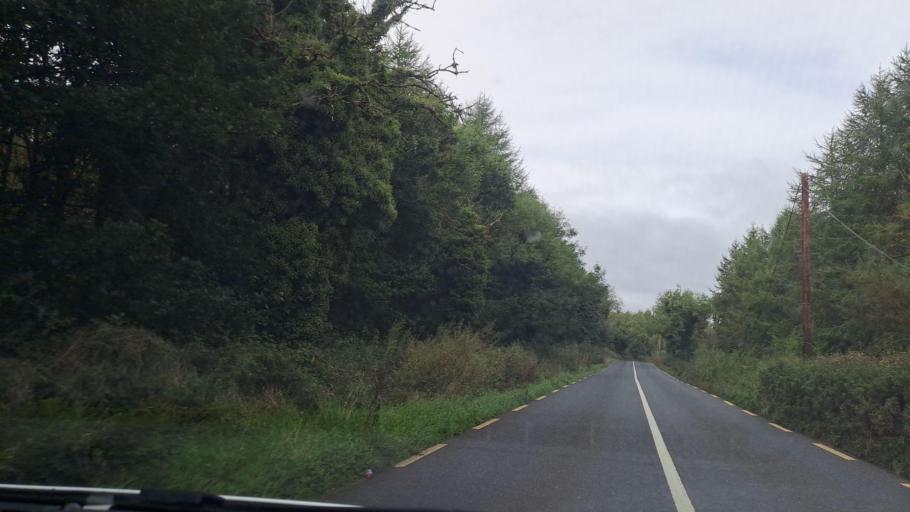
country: IE
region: Ulster
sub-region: County Monaghan
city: Carrickmacross
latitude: 53.8718
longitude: -6.7005
